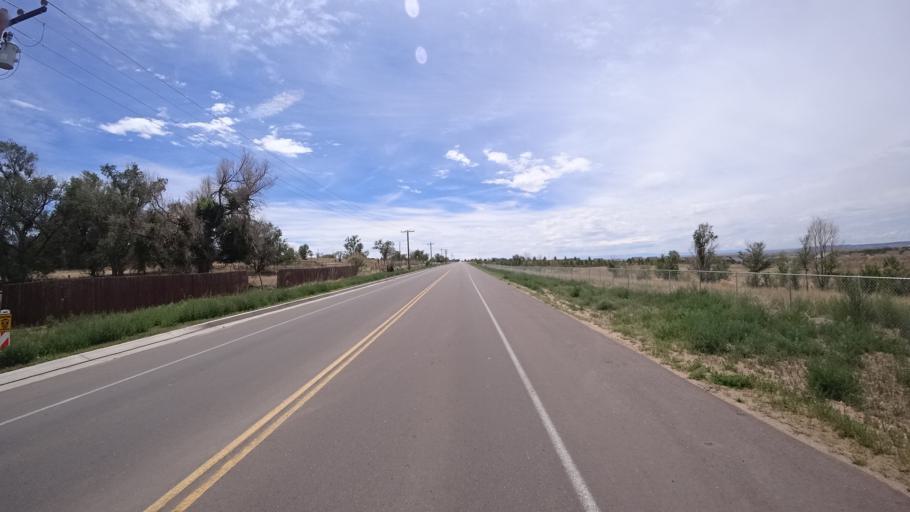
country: US
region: Colorado
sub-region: El Paso County
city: Fountain
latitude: 38.6971
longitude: -104.6736
